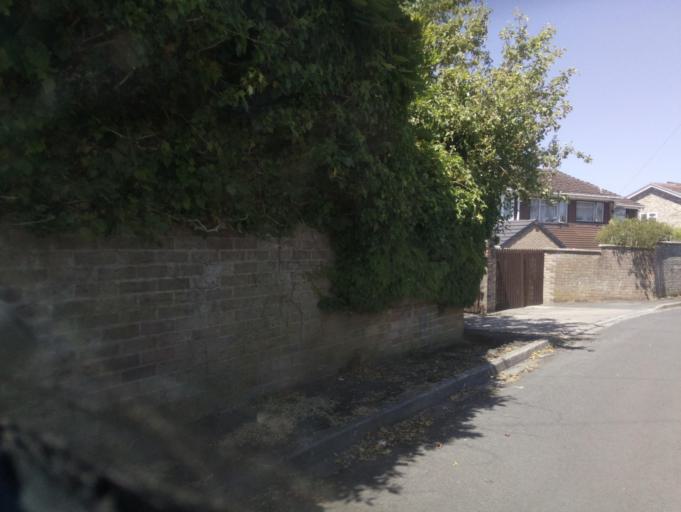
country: GB
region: England
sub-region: South Gloucestershire
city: Chipping Sodbury
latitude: 51.5321
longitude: -2.3994
